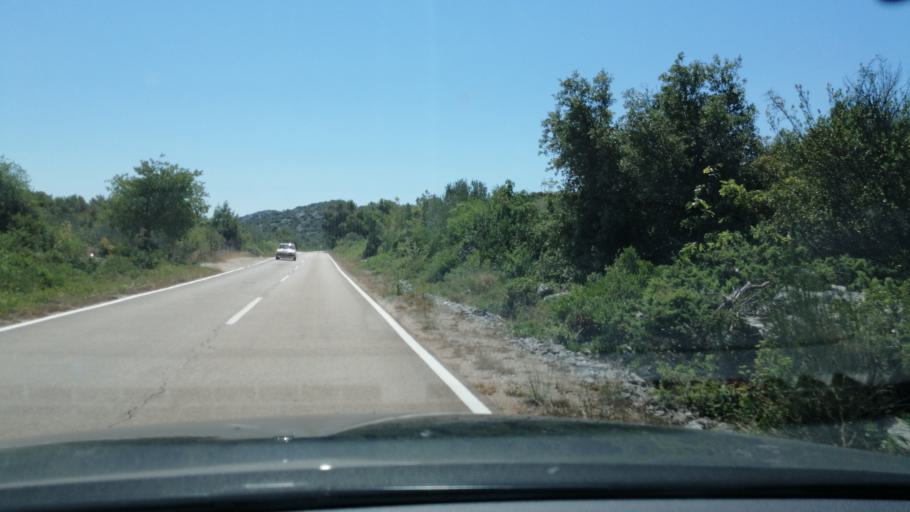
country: HR
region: Sibensko-Kniniska
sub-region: Grad Sibenik
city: Pirovac
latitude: 43.8427
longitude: 15.6879
